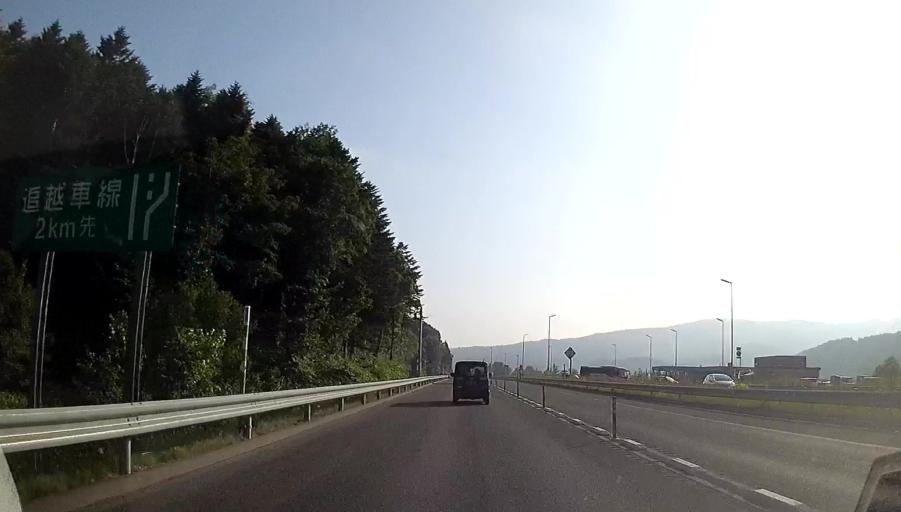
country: JP
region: Hokkaido
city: Shimo-furano
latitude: 43.0097
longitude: 142.4238
